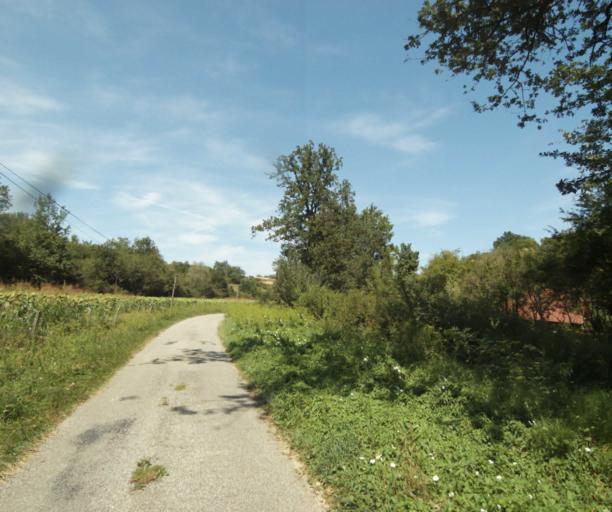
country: FR
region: Midi-Pyrenees
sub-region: Departement de l'Ariege
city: Lezat-sur-Leze
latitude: 43.2305
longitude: 1.3970
